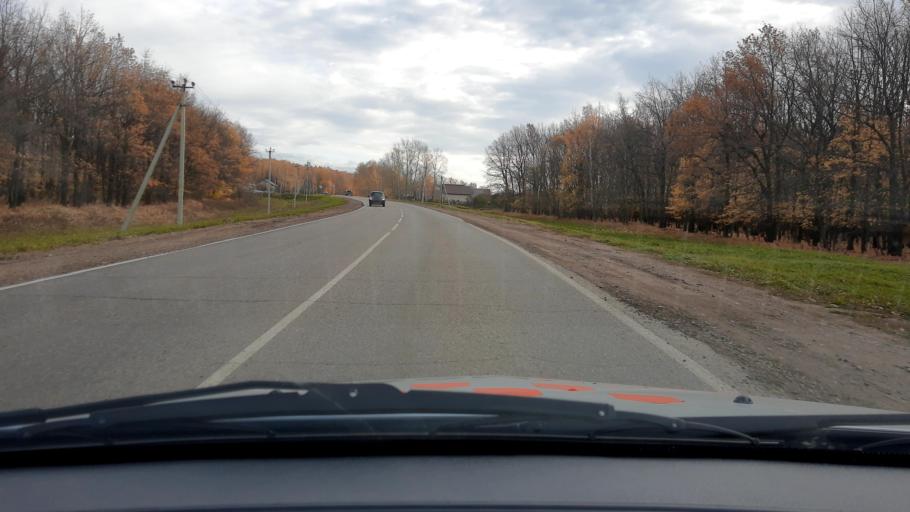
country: RU
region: Bashkortostan
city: Avdon
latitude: 54.8199
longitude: 55.7092
